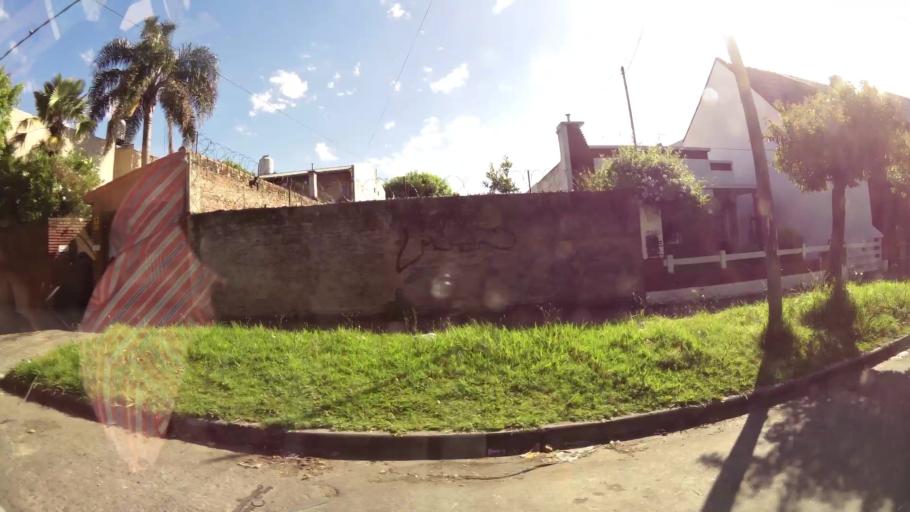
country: AR
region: Buenos Aires
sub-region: Partido de General San Martin
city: General San Martin
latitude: -34.5379
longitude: -58.5597
